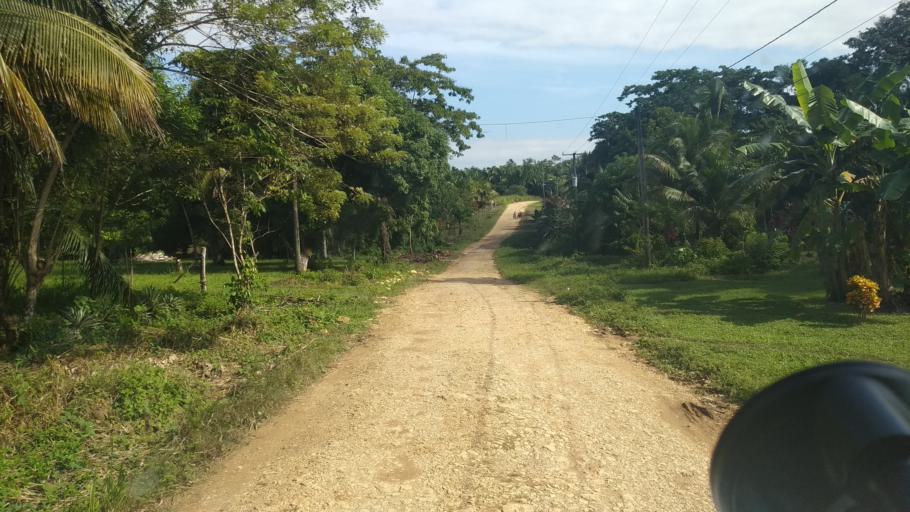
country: BZ
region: Toledo
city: Punta Gorda
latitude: 16.2136
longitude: -88.9098
